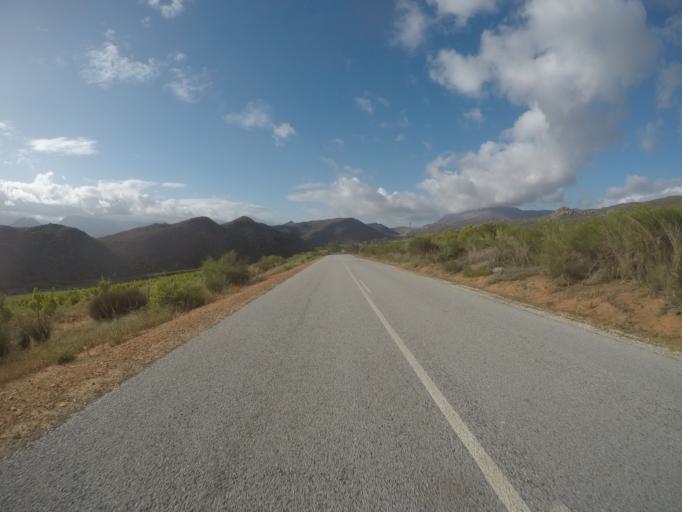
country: ZA
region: Western Cape
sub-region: West Coast District Municipality
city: Clanwilliam
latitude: -32.4286
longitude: 18.9377
